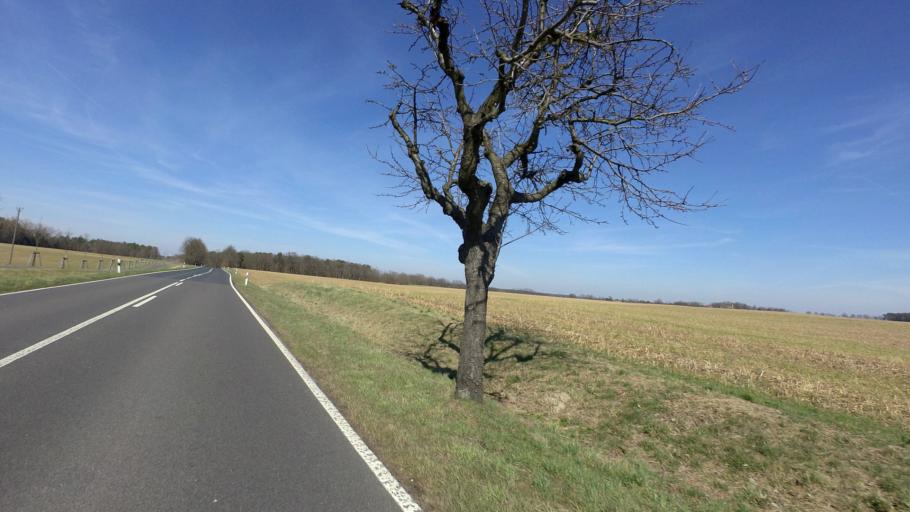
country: DE
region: Brandenburg
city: Furstenwalde
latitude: 52.3952
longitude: 14.0469
